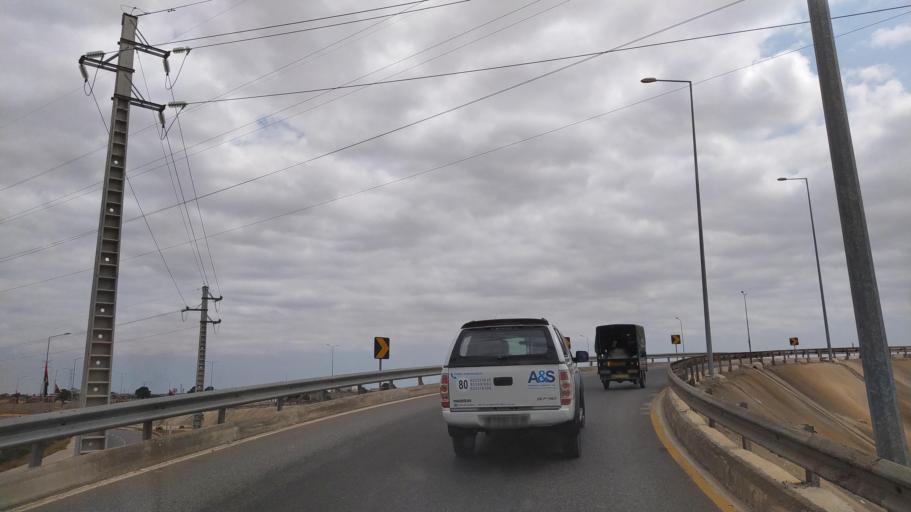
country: AO
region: Luanda
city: Luanda
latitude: -8.9748
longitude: 13.2544
